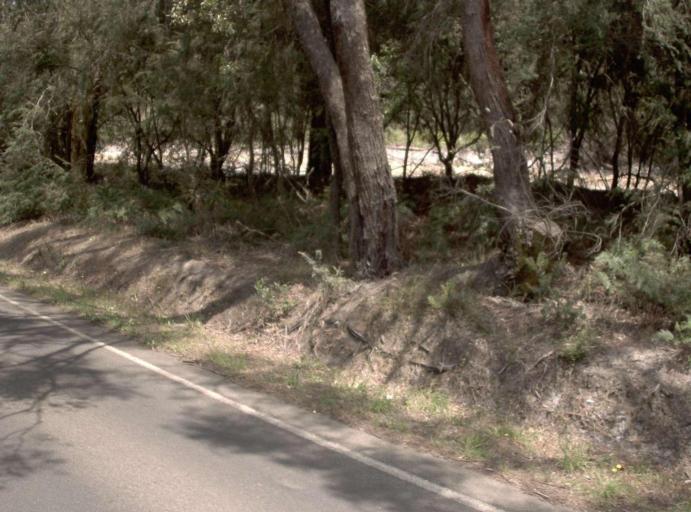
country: AU
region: Victoria
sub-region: Latrobe
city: Traralgon
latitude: -38.2720
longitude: 146.6922
